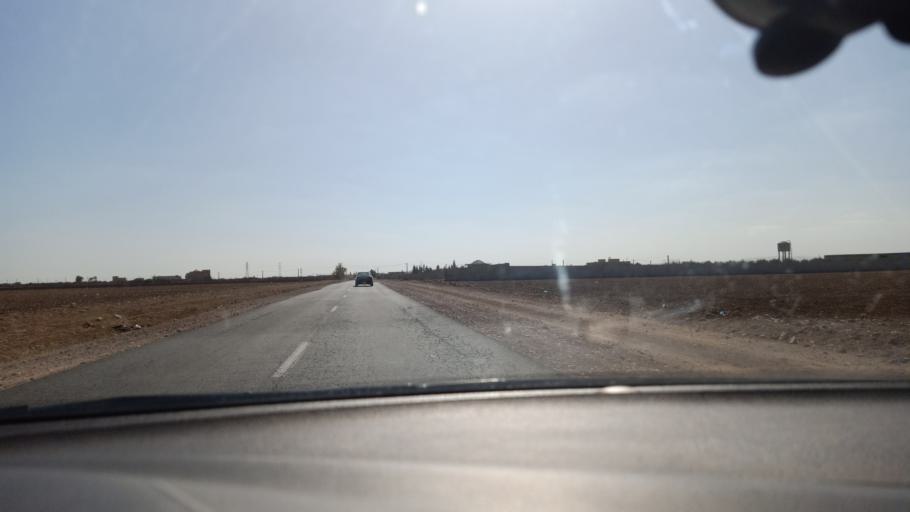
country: MA
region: Doukkala-Abda
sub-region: Safi
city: Youssoufia
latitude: 32.1210
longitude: -8.6038
